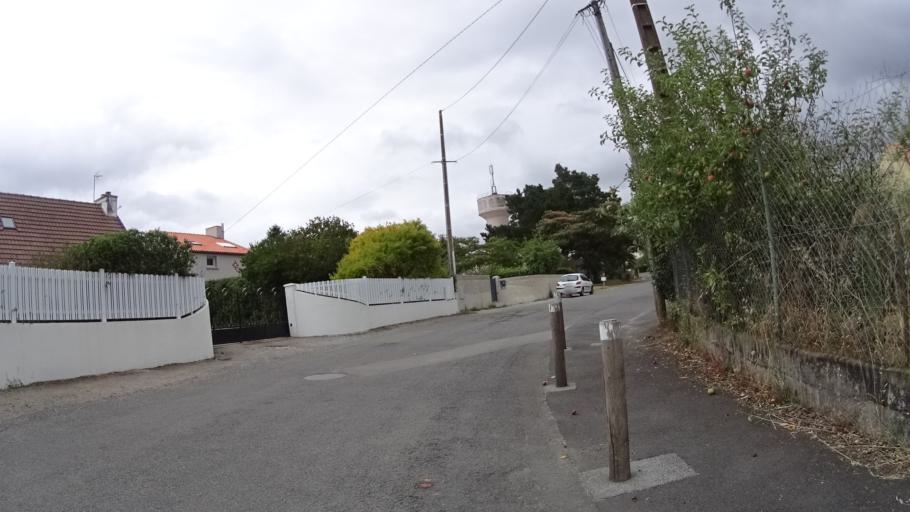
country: FR
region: Pays de la Loire
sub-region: Departement de la Loire-Atlantique
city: Saint-Jean-de-Boiseau
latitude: 47.1952
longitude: -1.7101
